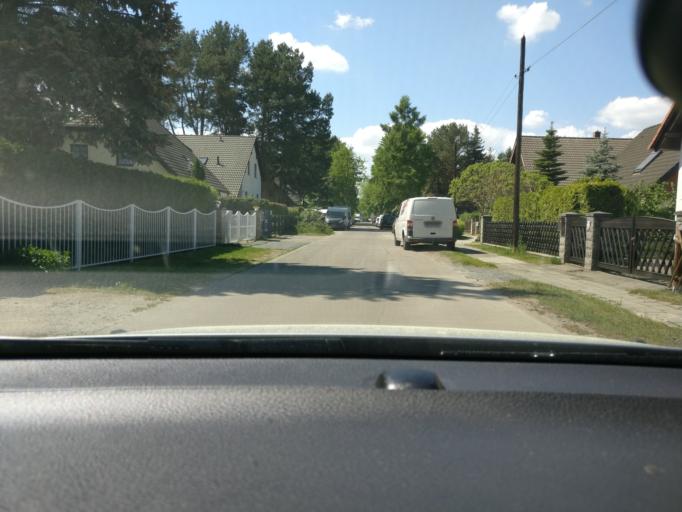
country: DE
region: Berlin
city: Muggelheim
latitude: 52.4134
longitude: 13.6693
